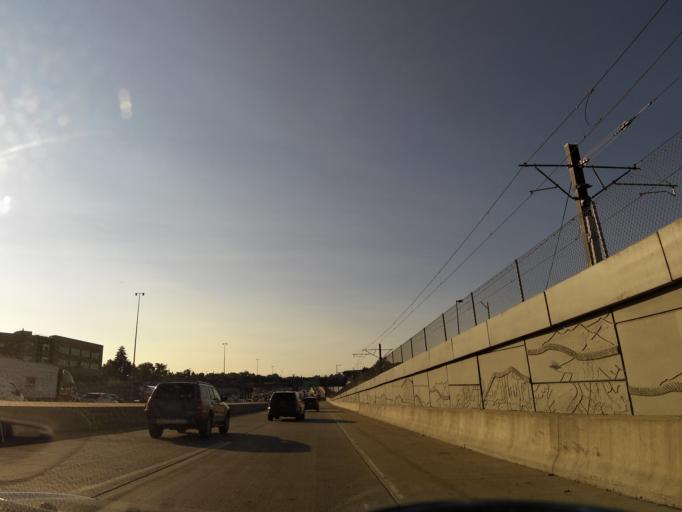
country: US
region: Colorado
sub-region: Denver County
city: Denver
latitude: 39.6988
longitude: -104.9849
